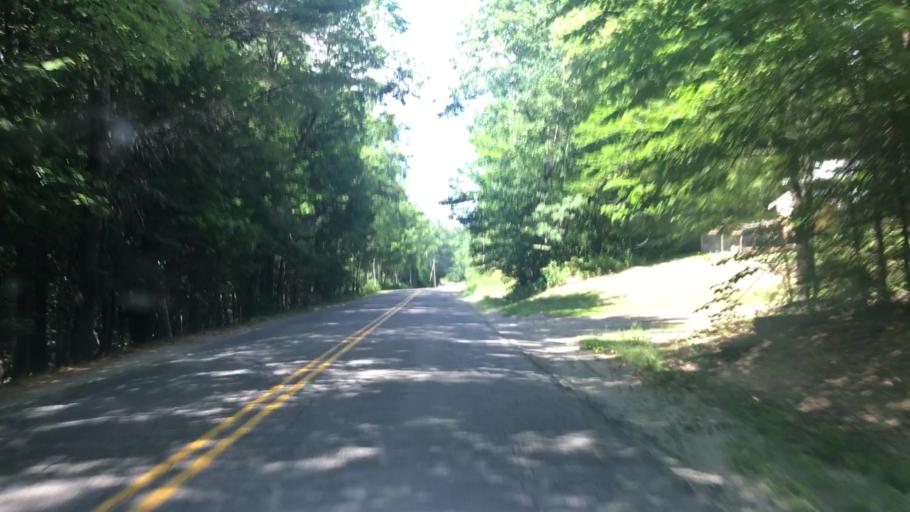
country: US
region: Maine
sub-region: Franklin County
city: Chesterville
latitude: 44.5632
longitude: -70.0863
